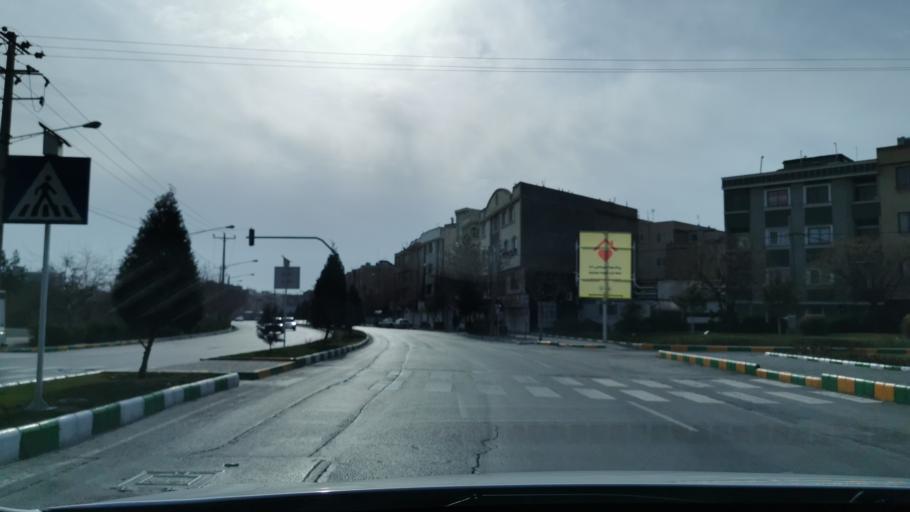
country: IR
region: Razavi Khorasan
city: Mashhad
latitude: 36.3142
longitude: 59.5118
